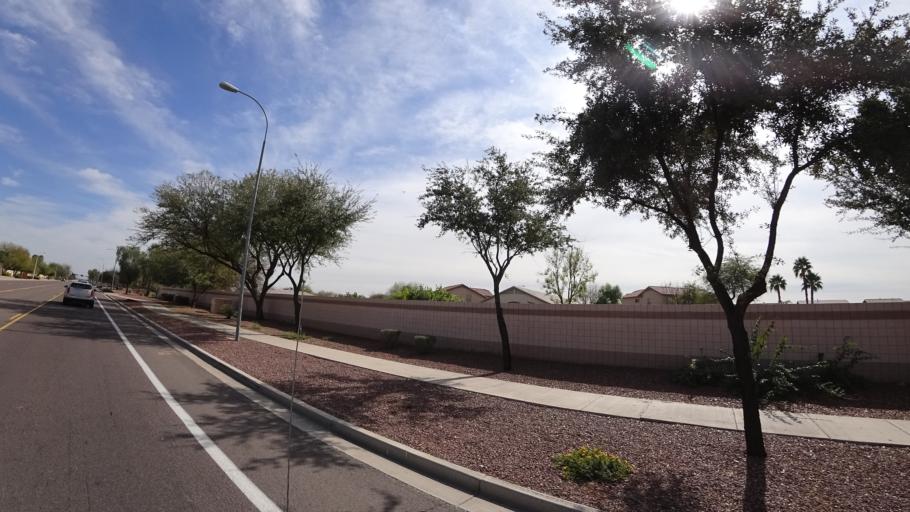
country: US
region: Arizona
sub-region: Maricopa County
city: Tolleson
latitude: 33.4788
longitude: -112.2955
